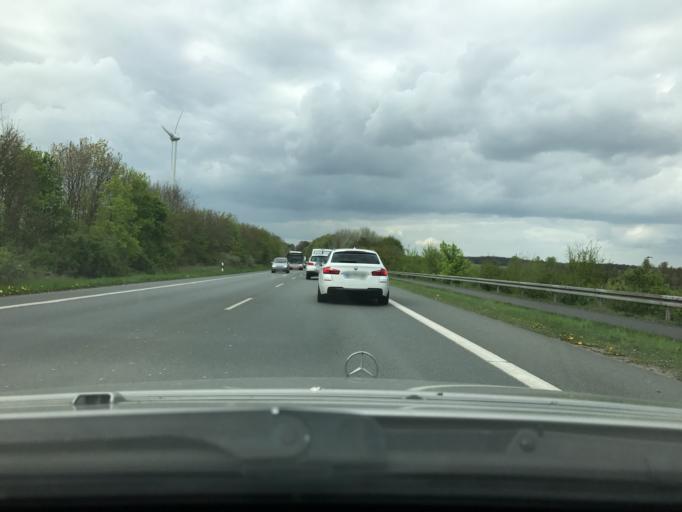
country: DE
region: North Rhine-Westphalia
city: Waltrop
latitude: 51.5932
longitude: 7.3928
